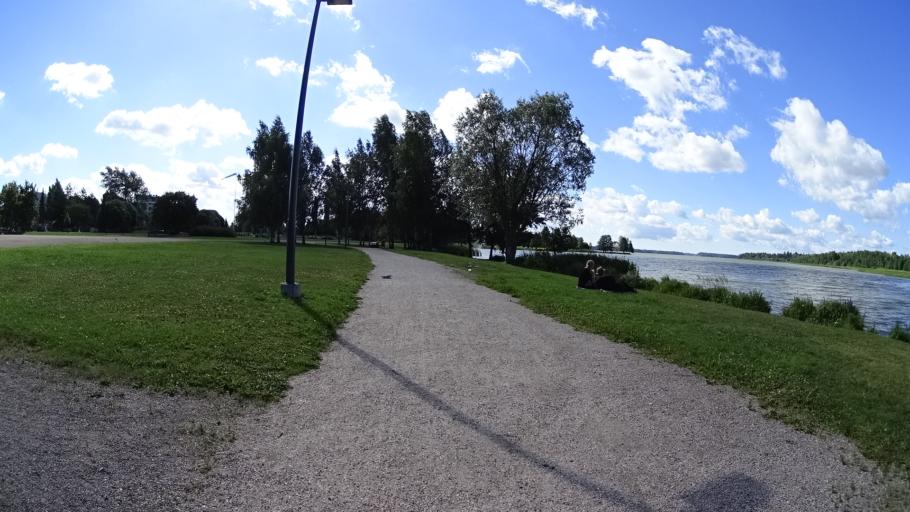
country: FI
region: Uusimaa
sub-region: Helsinki
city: Jaervenpaeae
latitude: 60.4685
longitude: 25.0818
